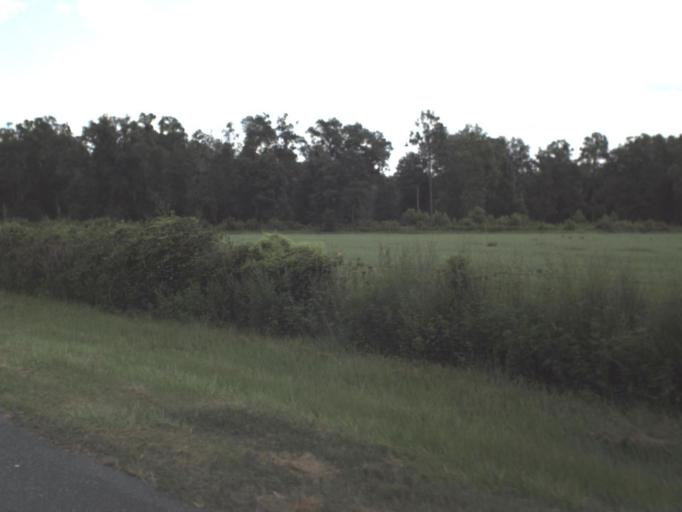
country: US
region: Florida
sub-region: Union County
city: Lake Butler
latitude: 29.9614
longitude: -82.4098
